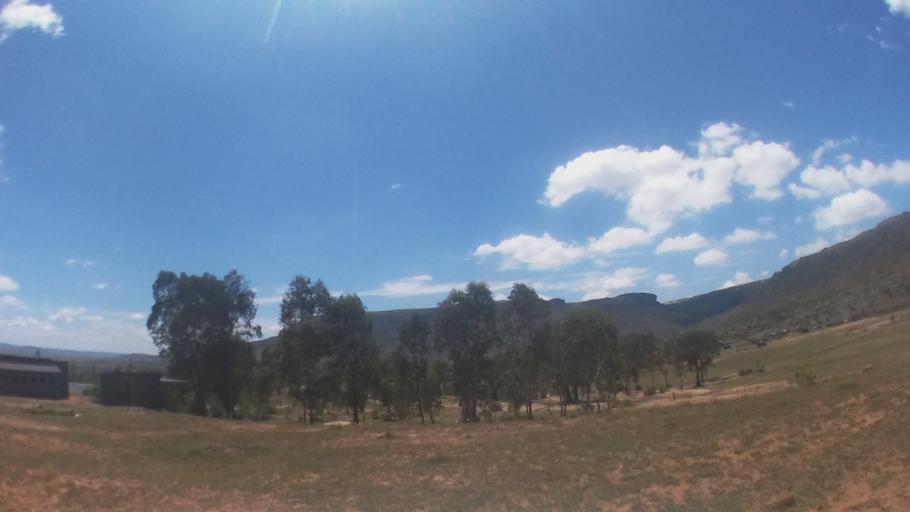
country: LS
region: Maseru
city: Maseru
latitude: -29.4396
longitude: 27.4140
